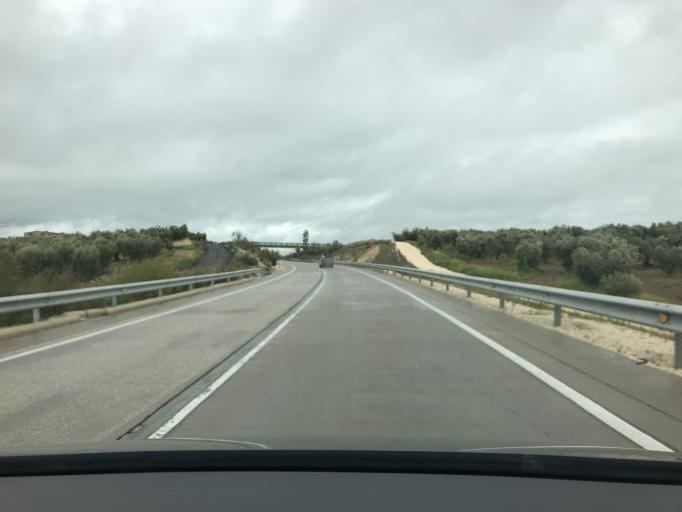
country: ES
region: Andalusia
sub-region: Provincia de Sevilla
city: Marchena
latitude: 37.3018
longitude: -5.4166
